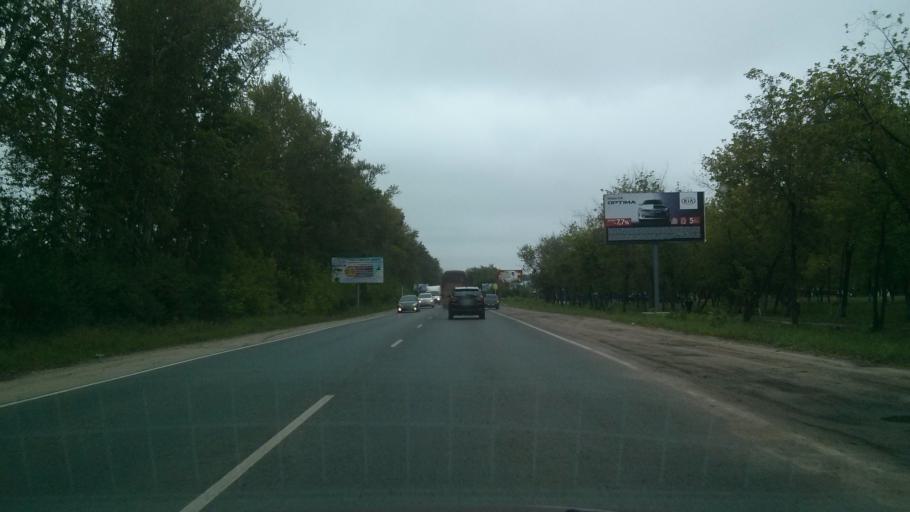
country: RU
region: Vladimir
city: Murom
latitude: 55.5990
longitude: 42.0323
